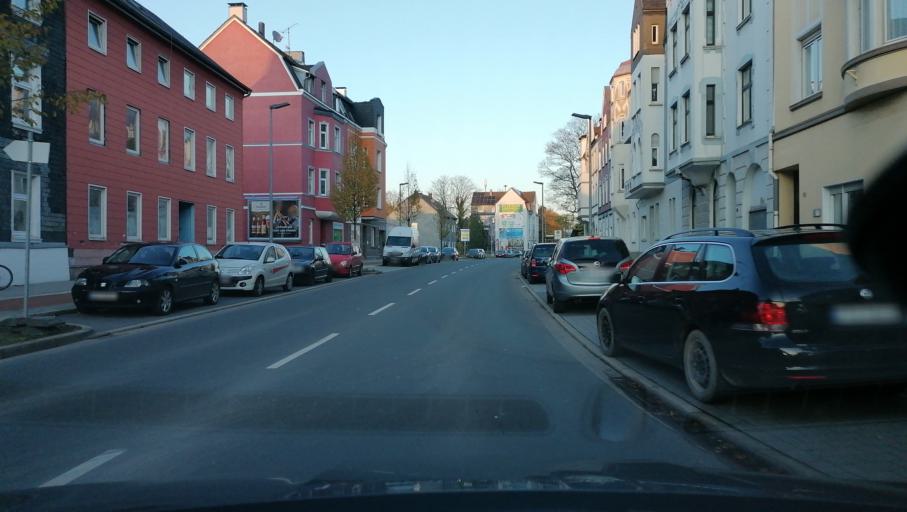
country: DE
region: North Rhine-Westphalia
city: Gevelsberg
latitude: 51.3242
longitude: 7.3499
